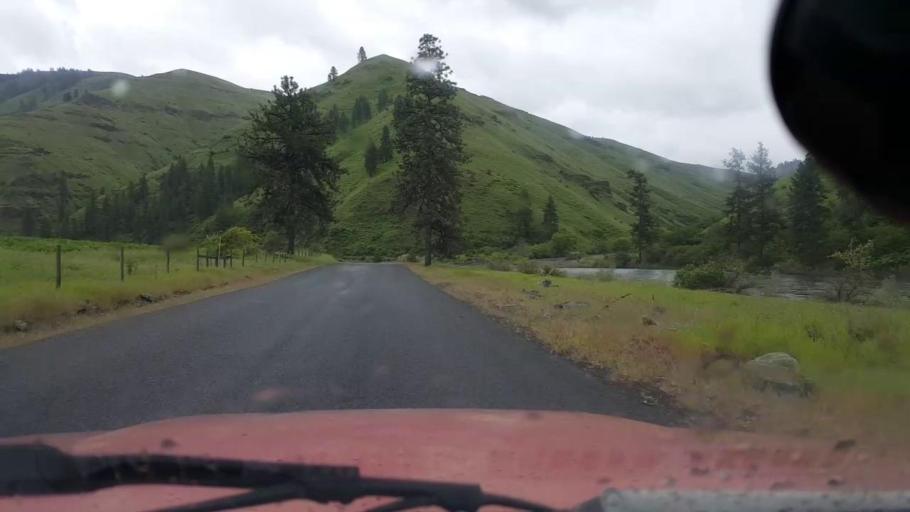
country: US
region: Washington
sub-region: Asotin County
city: Asotin
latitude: 46.0299
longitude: -117.3159
